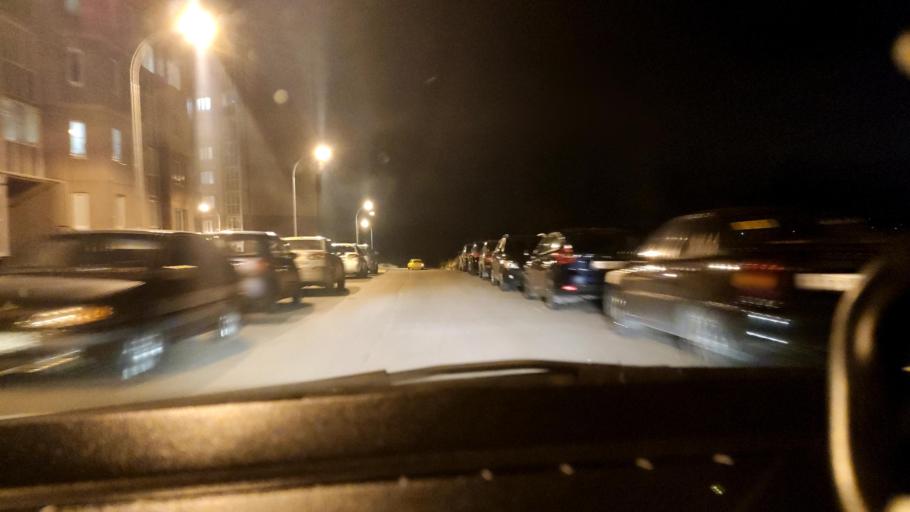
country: RU
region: Voronezj
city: Shilovo
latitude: 51.5740
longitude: 39.1296
